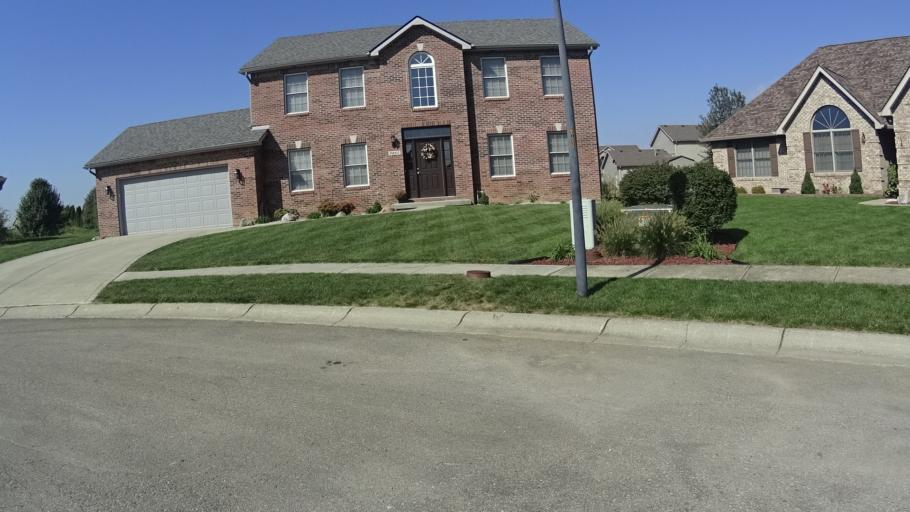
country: US
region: Indiana
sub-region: Madison County
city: Lapel
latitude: 40.0586
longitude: -85.8511
